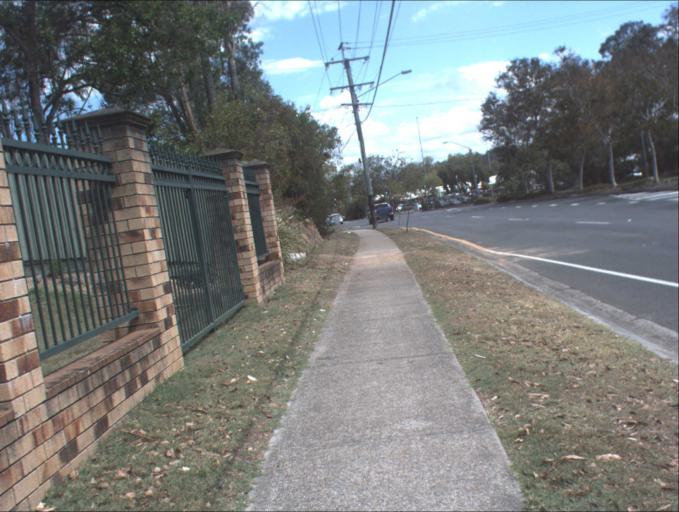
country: AU
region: Queensland
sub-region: Logan
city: Slacks Creek
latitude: -27.6580
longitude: 153.1734
